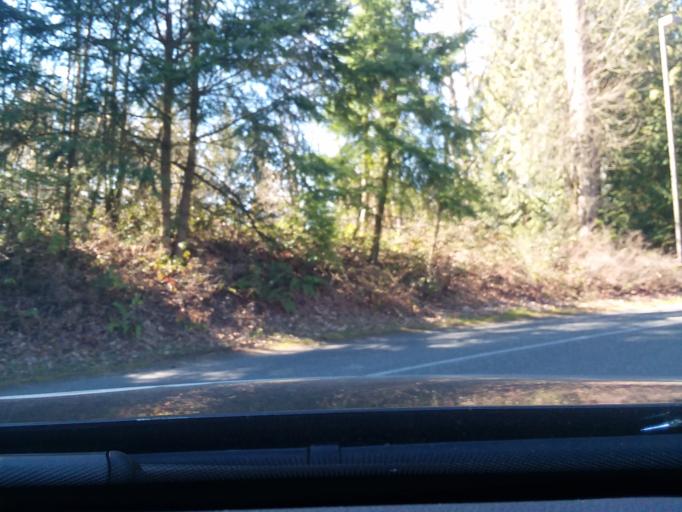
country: US
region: Washington
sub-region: Pierce County
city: South Hill
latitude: 47.1549
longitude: -122.2719
